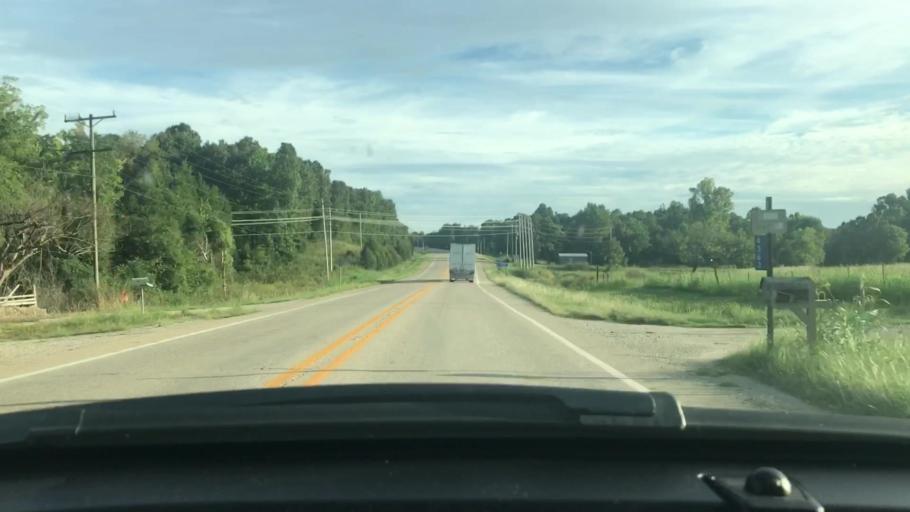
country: US
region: Arkansas
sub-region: Lawrence County
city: Hoxie
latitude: 36.1370
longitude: -91.1582
